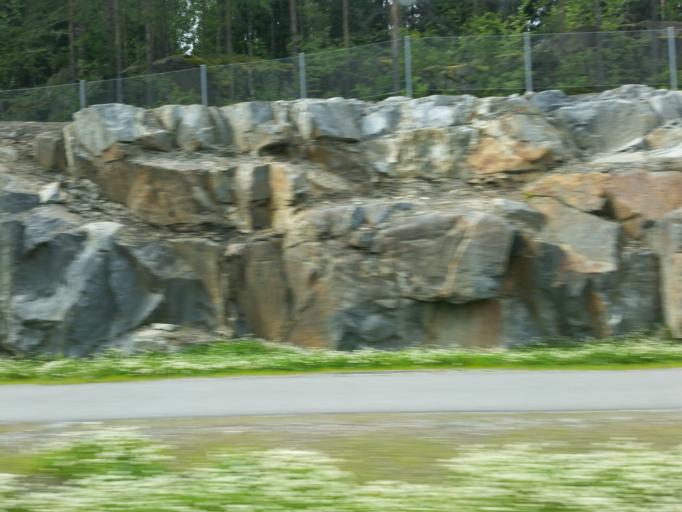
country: FI
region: Northern Savo
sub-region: Kuopio
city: Kuopio
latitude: 62.9711
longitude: 27.7046
